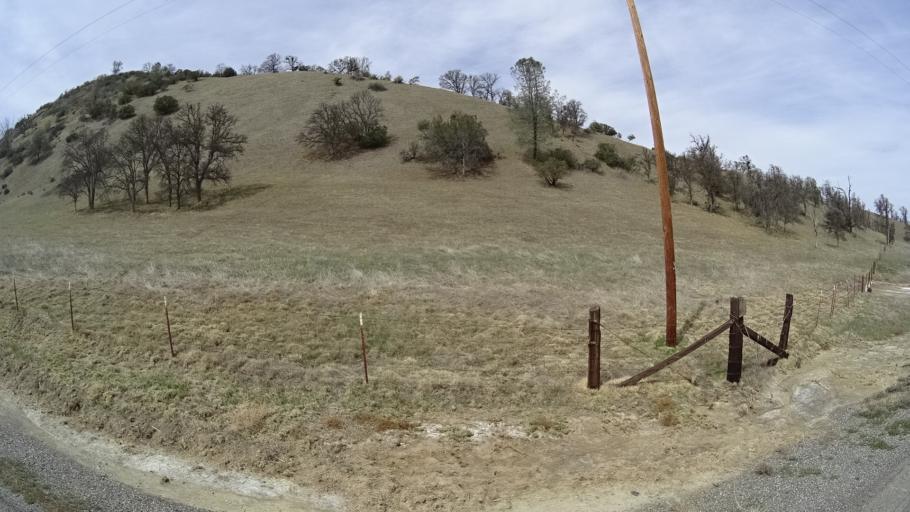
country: US
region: California
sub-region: Glenn County
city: Willows
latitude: 39.4230
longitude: -122.5323
